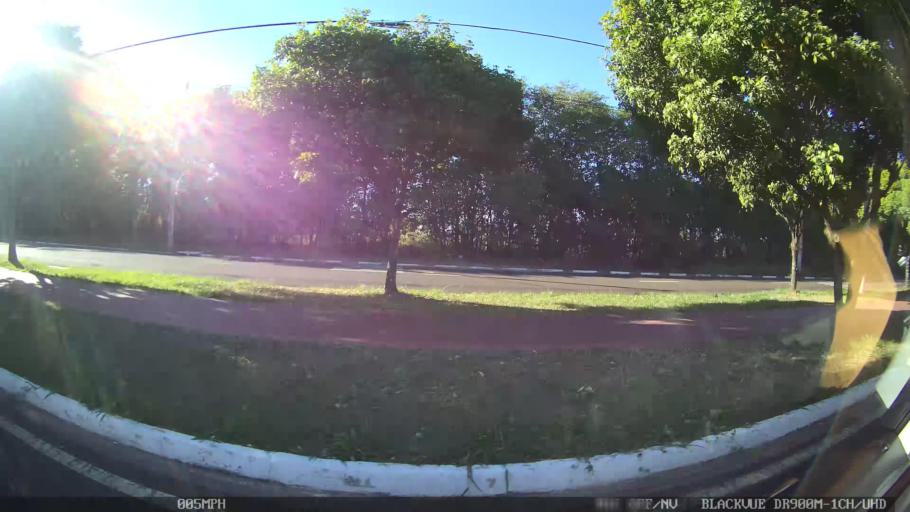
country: BR
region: Sao Paulo
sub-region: Franca
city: Franca
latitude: -20.5704
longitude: -47.3673
